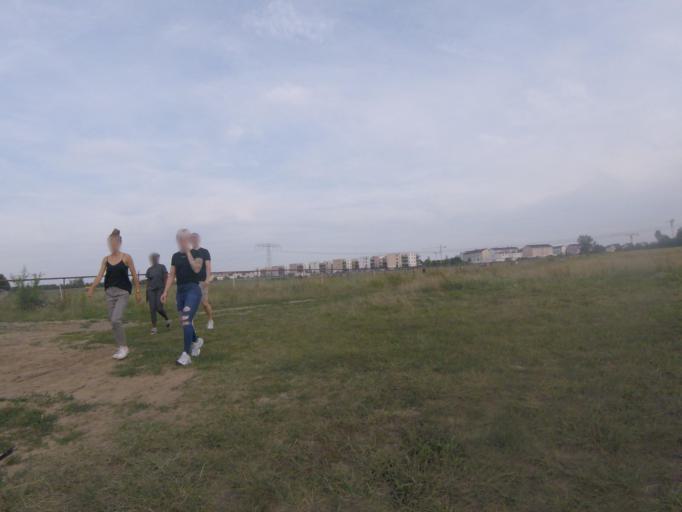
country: DE
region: Berlin
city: Rudow
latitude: 52.3973
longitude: 13.4922
